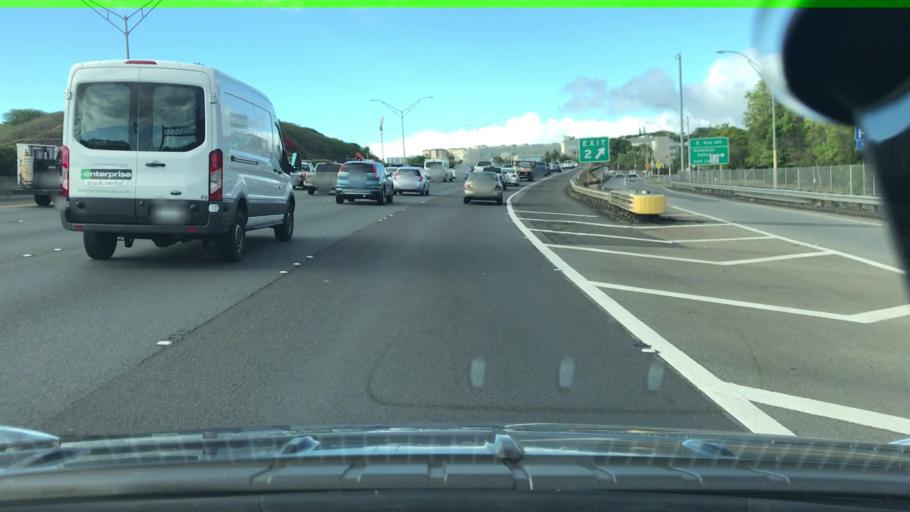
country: US
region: Hawaii
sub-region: Honolulu County
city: Halawa Heights
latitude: 21.3578
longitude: -157.8992
